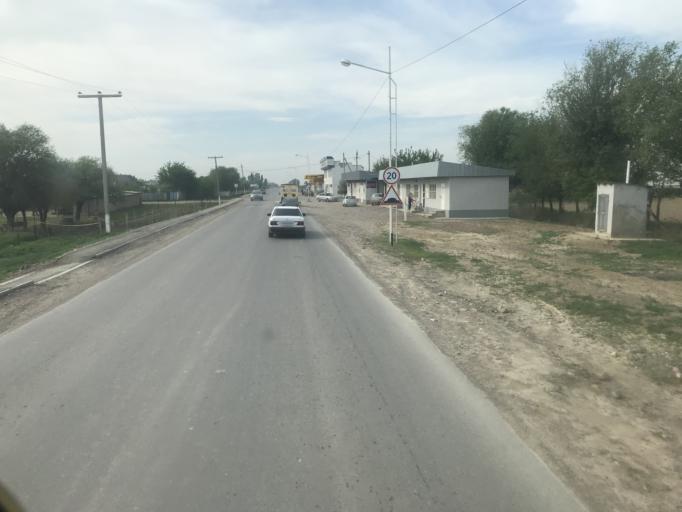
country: KZ
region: Ongtustik Qazaqstan
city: Asykata
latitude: 41.0037
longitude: 68.2142
